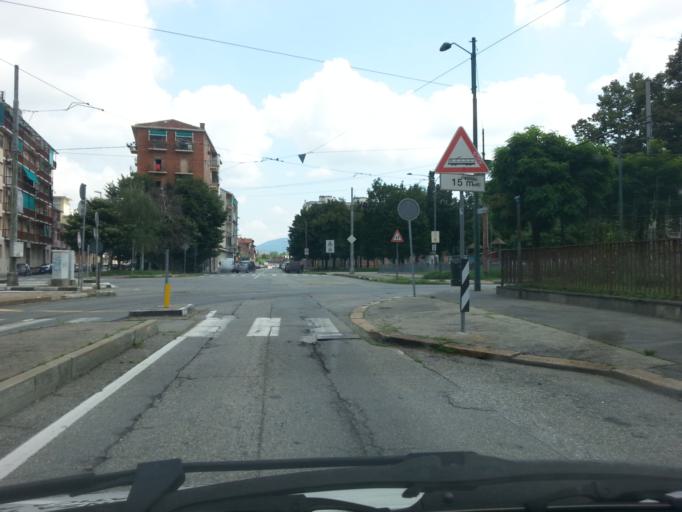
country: IT
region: Piedmont
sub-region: Provincia di Torino
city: Turin
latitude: 45.1062
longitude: 7.6814
